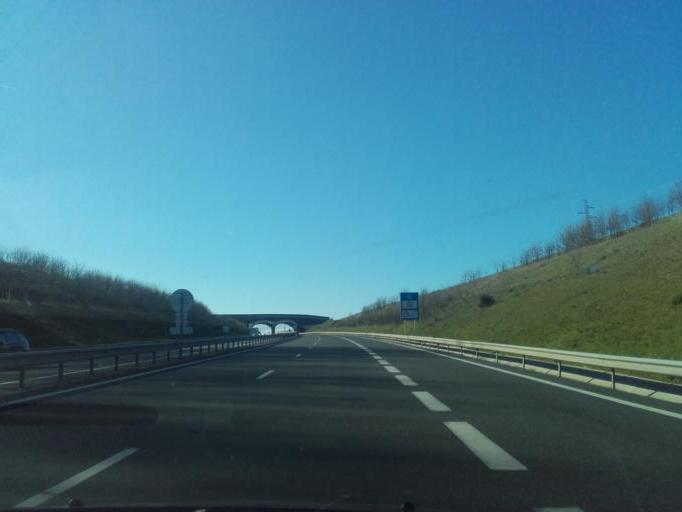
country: FR
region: Rhone-Alpes
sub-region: Departement de l'Ain
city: Beynost
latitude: 45.8490
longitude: 5.0107
